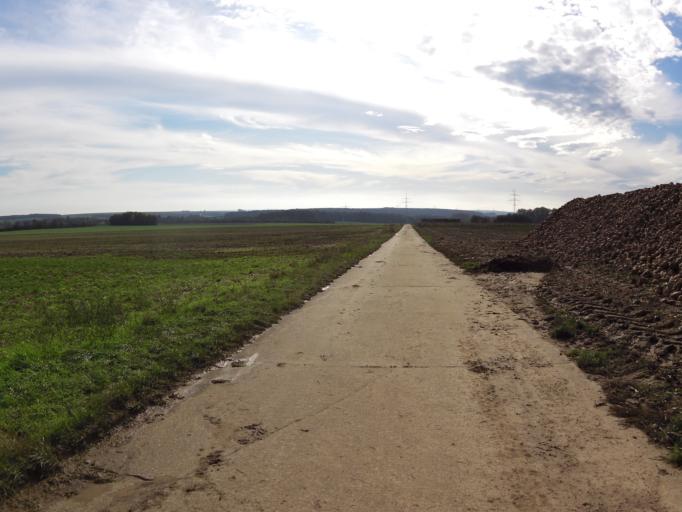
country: DE
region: Bavaria
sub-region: Regierungsbezirk Unterfranken
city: Sommerhausen
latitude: 49.7156
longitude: 10.0689
